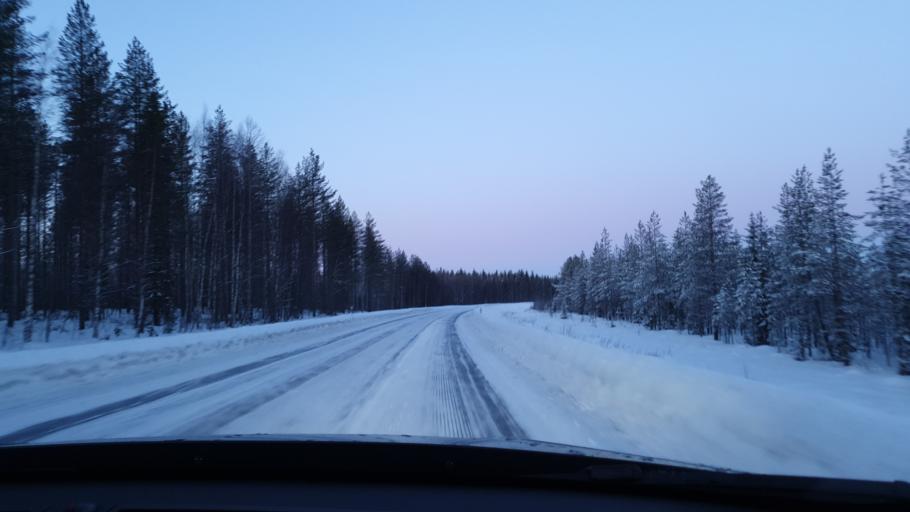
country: FI
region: Kainuu
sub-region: Kehys-Kainuu
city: Kuhmo
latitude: 64.0917
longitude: 29.4090
